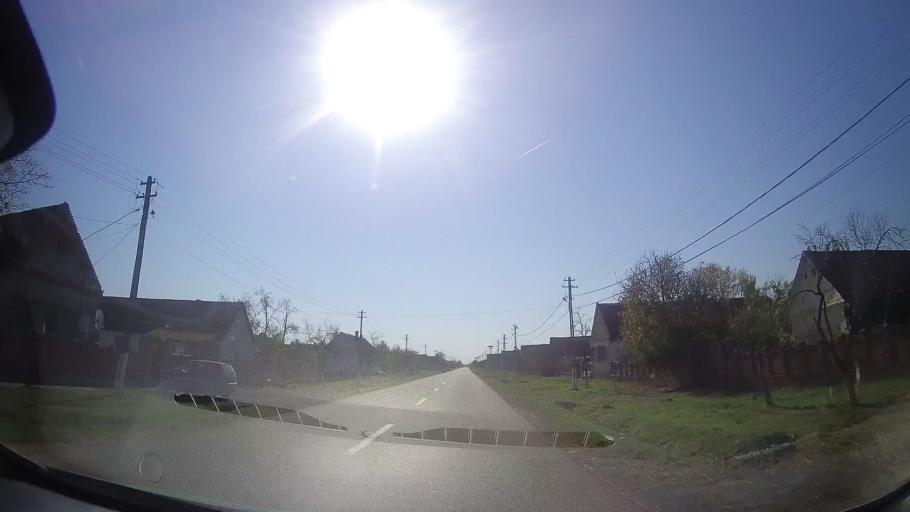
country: RO
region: Timis
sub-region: Comuna Ghizela
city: Ghizela
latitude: 45.8033
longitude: 21.7236
